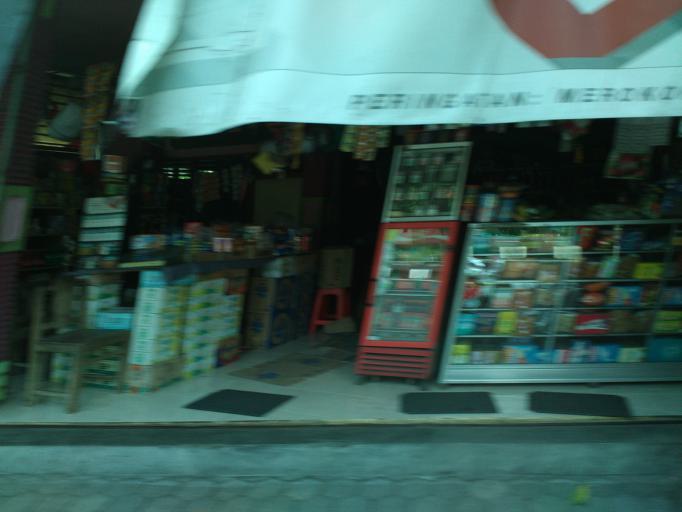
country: ID
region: Central Java
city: Candi Prambanan
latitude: -7.7458
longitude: 110.5263
